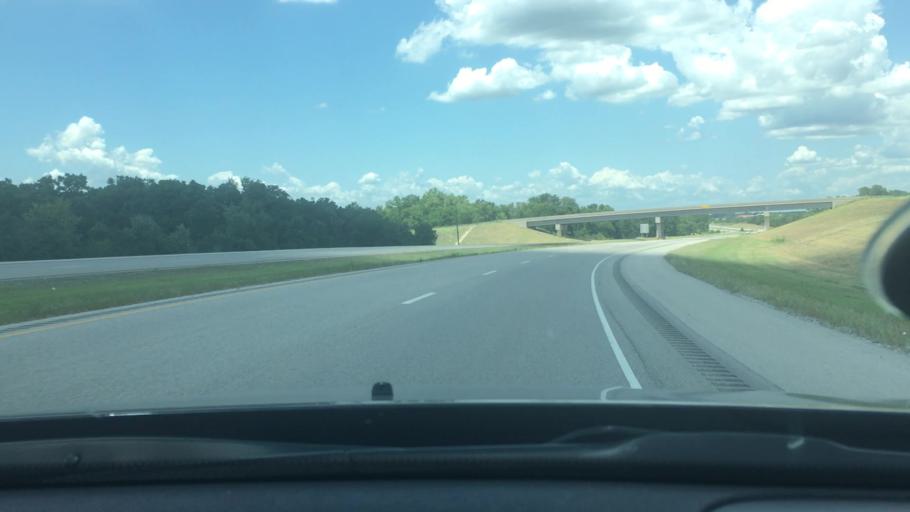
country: US
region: Oklahoma
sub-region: Bryan County
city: Calera
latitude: 33.9807
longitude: -96.4274
